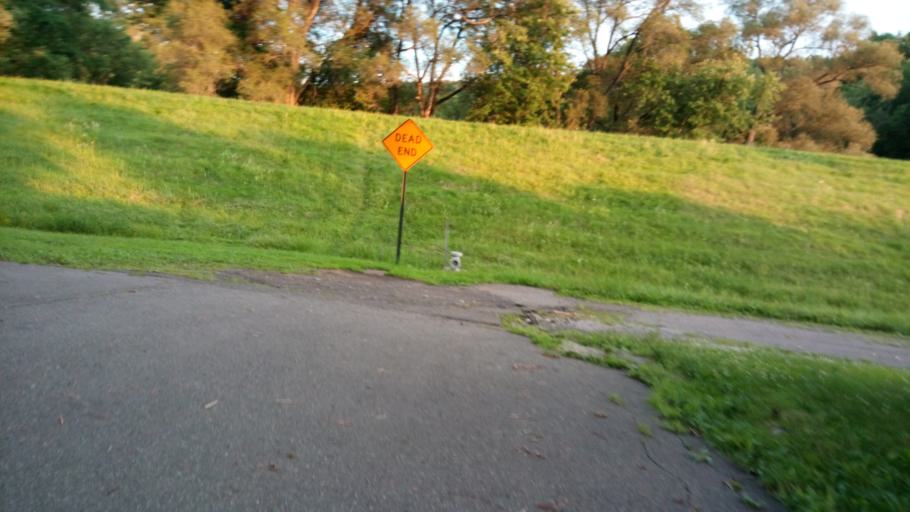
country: US
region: New York
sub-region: Chemung County
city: West Elmira
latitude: 42.0749
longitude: -76.8431
